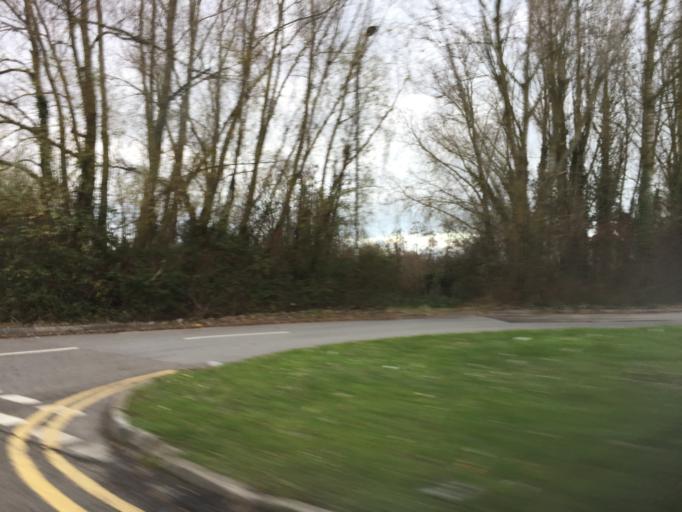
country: GB
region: Wales
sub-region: Newport
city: Bishton
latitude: 51.5735
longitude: -2.8628
